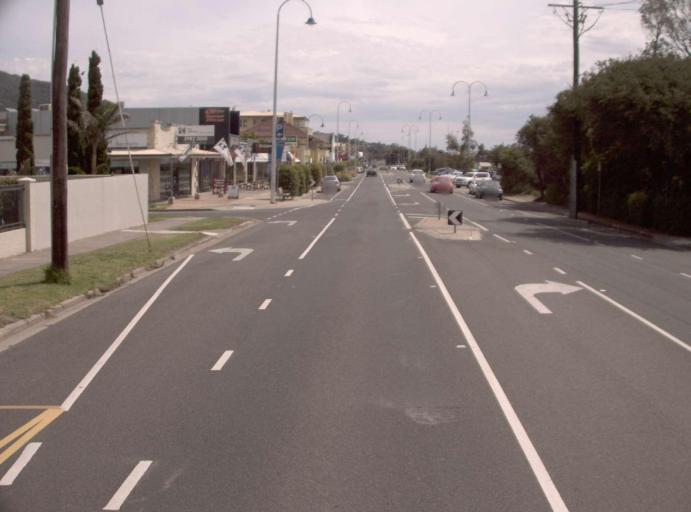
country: AU
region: Victoria
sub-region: Mornington Peninsula
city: Dromana
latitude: -38.3306
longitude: 144.9691
